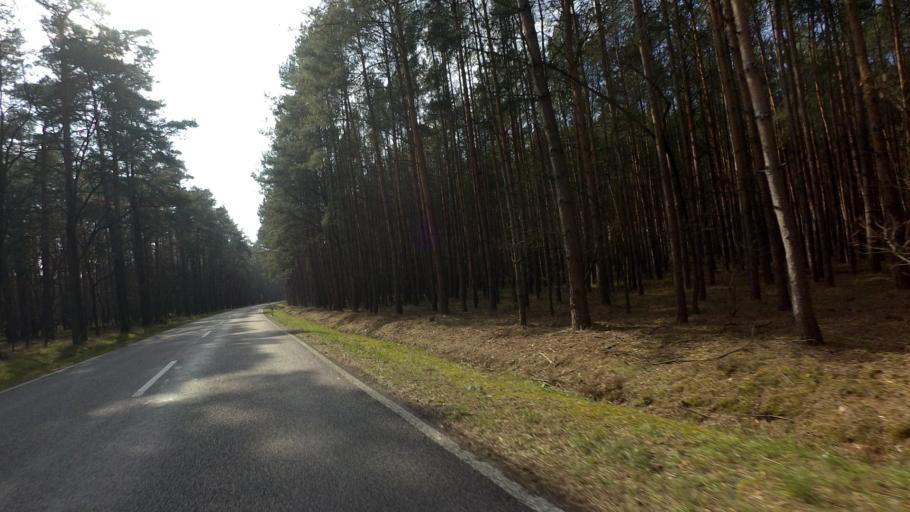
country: DE
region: Brandenburg
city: Dahme
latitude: 51.9556
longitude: 13.4174
